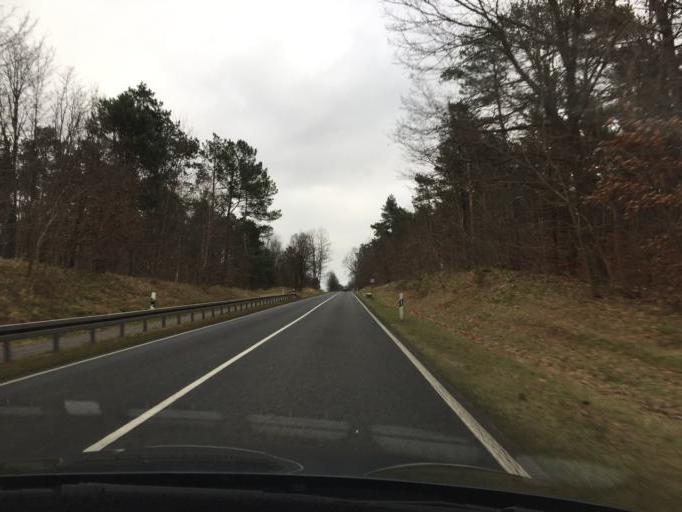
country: DE
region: Brandenburg
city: Ziltendorf
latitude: 52.1482
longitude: 14.5683
